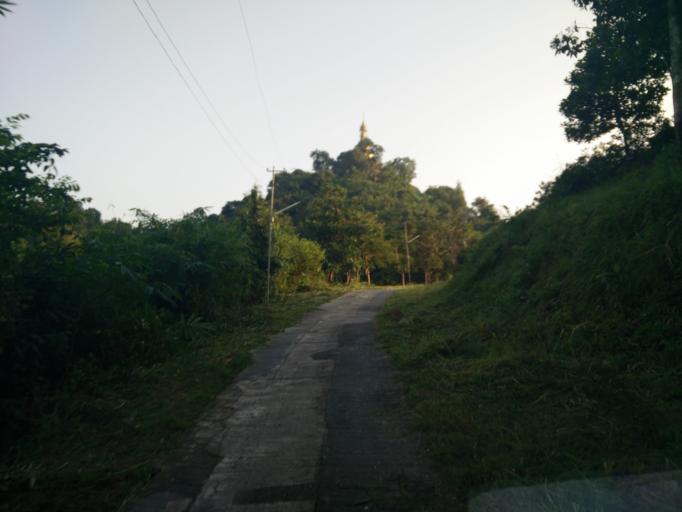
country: MM
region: Mon
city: Thaton
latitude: 16.9274
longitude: 97.3821
